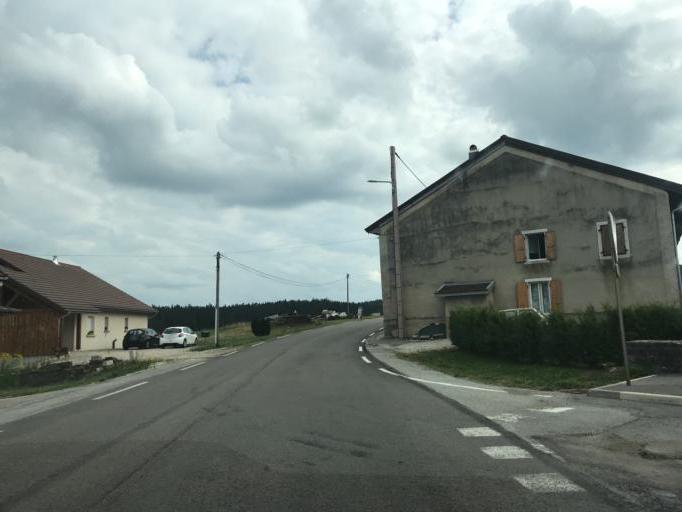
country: FR
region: Franche-Comte
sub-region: Departement du Jura
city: Valfin-les-Saint-Claude
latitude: 46.5077
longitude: 5.8676
